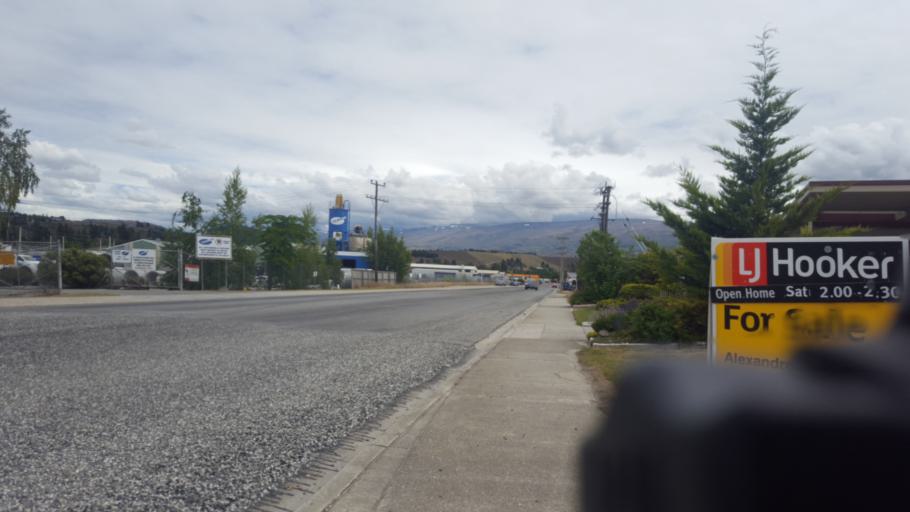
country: NZ
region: Otago
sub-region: Queenstown-Lakes District
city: Wanaka
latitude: -45.2461
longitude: 169.3760
